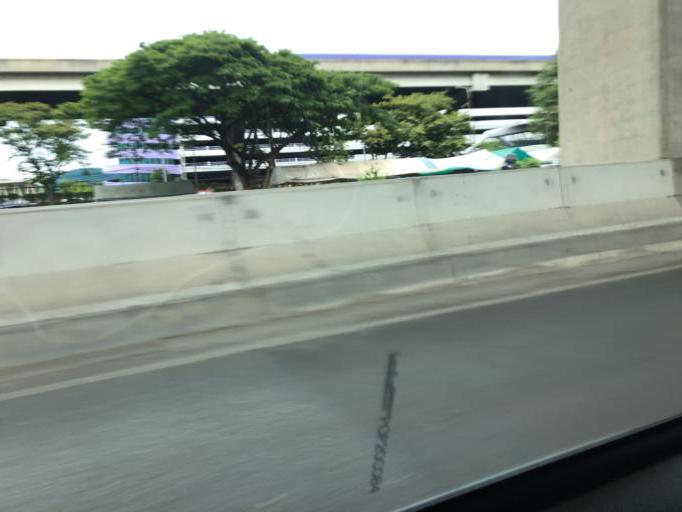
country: TH
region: Bangkok
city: Don Mueang
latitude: 13.9326
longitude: 100.6078
